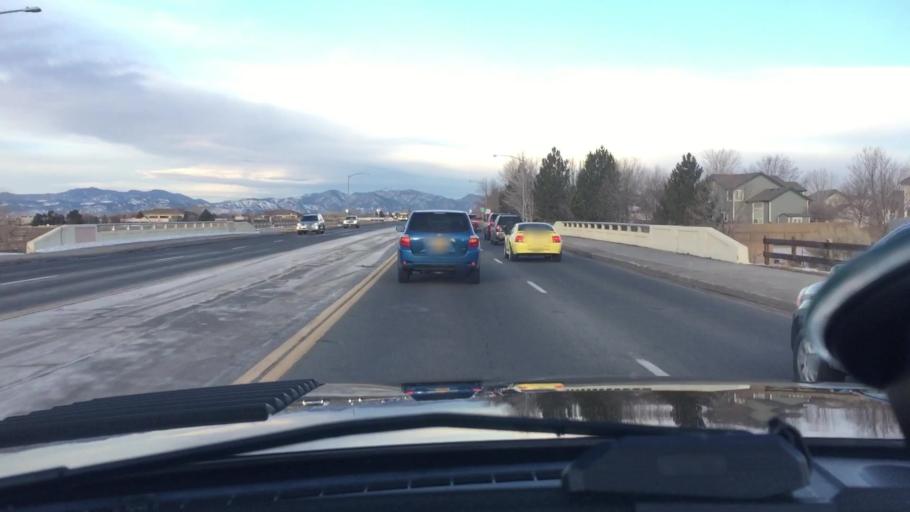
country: US
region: Colorado
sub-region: Broomfield County
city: Broomfield
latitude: 39.8998
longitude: -105.0466
